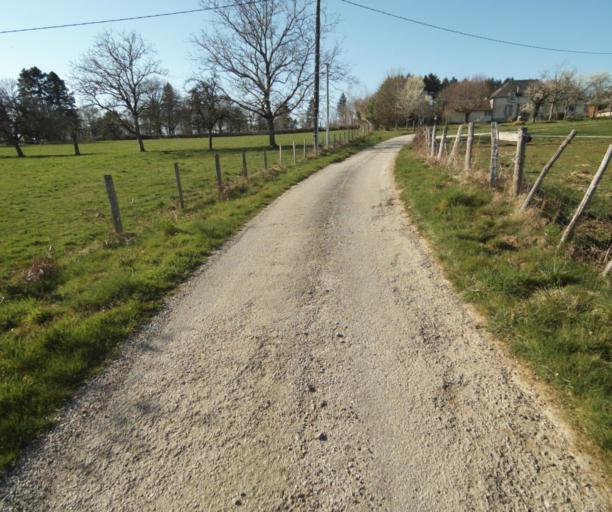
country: FR
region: Limousin
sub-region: Departement de la Correze
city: Chamboulive
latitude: 45.4725
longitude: 1.7044
